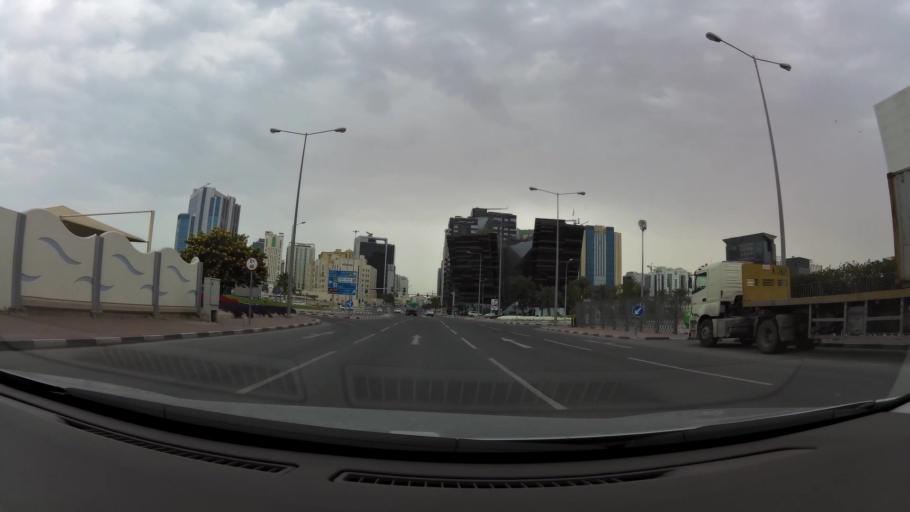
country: QA
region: Baladiyat ad Dawhah
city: Doha
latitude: 25.2930
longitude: 51.5441
